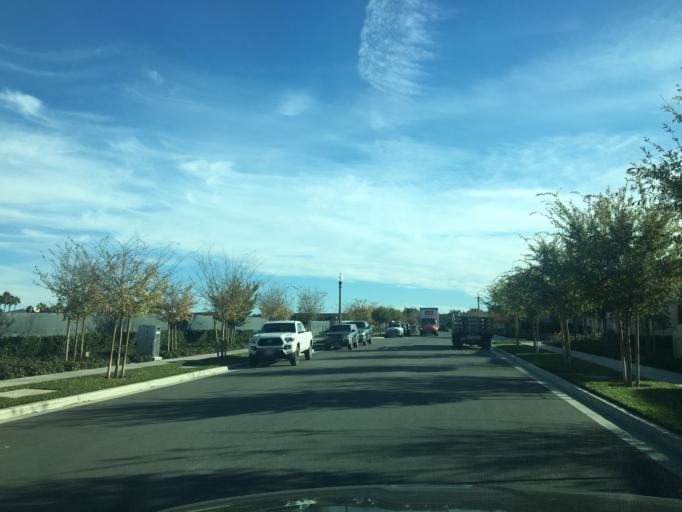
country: US
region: California
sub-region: Orange County
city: Laguna Woods
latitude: 33.6391
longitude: -117.7437
